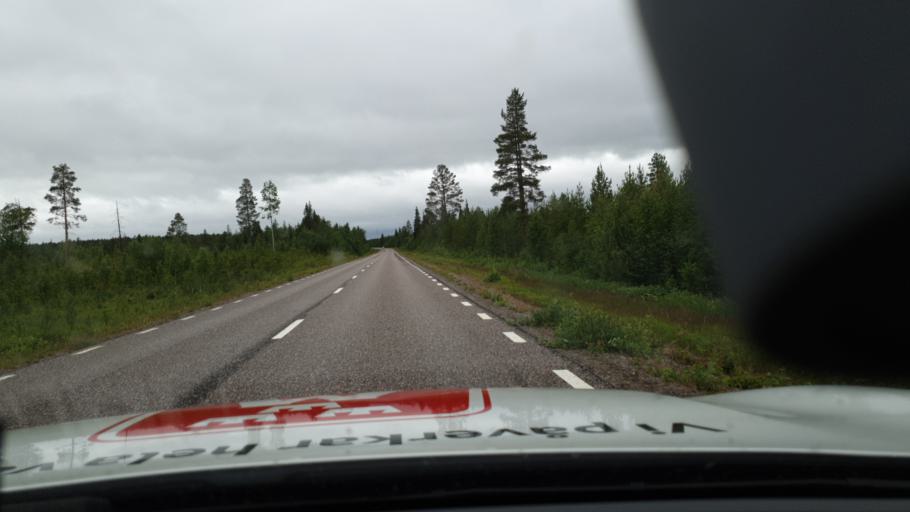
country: SE
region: Norrbotten
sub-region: Pajala Kommun
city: Pajala
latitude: 67.1531
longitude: 23.5561
